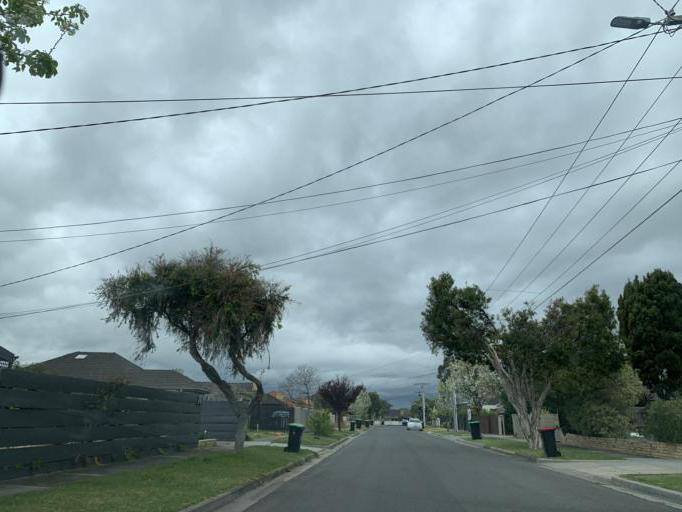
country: AU
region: Victoria
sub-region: Kingston
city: Mentone
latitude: -37.9717
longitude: 145.0699
